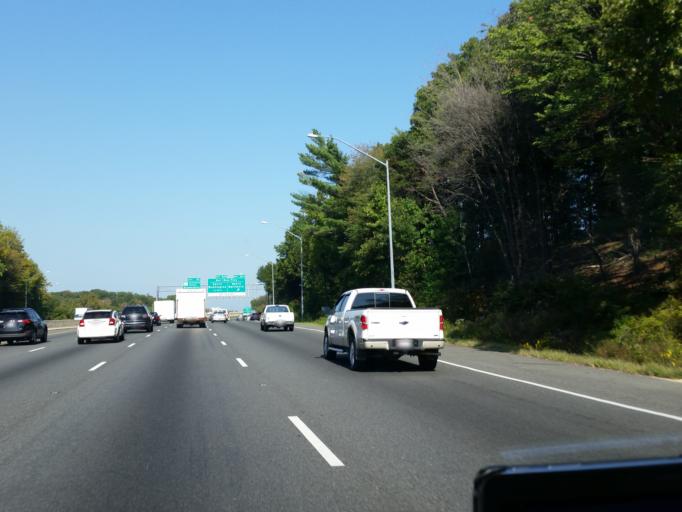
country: US
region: Maryland
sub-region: Prince George's County
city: New Carrollton
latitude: 38.9877
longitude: -76.8823
